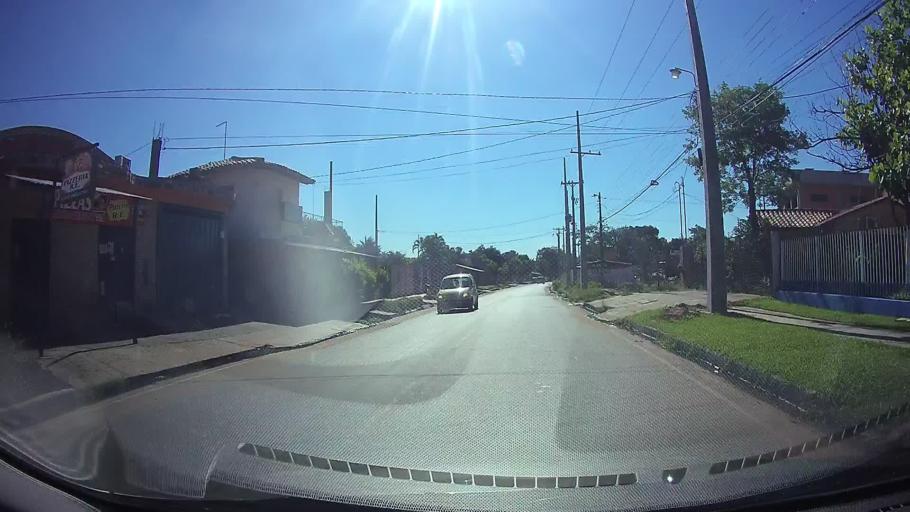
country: PY
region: Central
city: Fernando de la Mora
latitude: -25.2967
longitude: -57.5260
